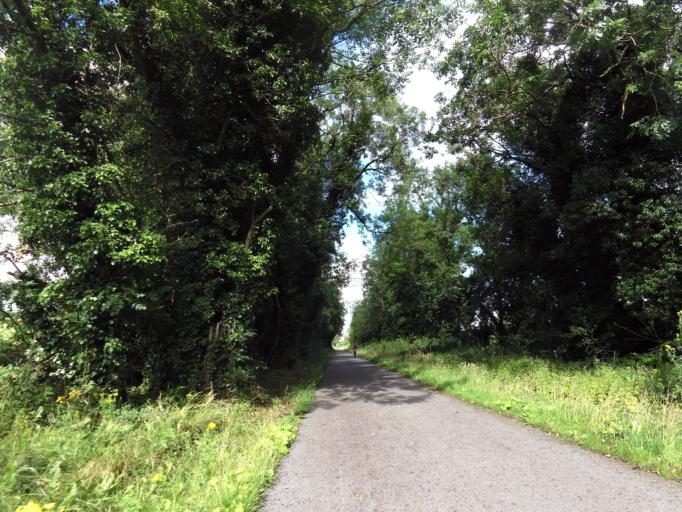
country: IE
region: Leinster
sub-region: An Iarmhi
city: Kilbeggan
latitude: 53.4398
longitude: -7.5575
